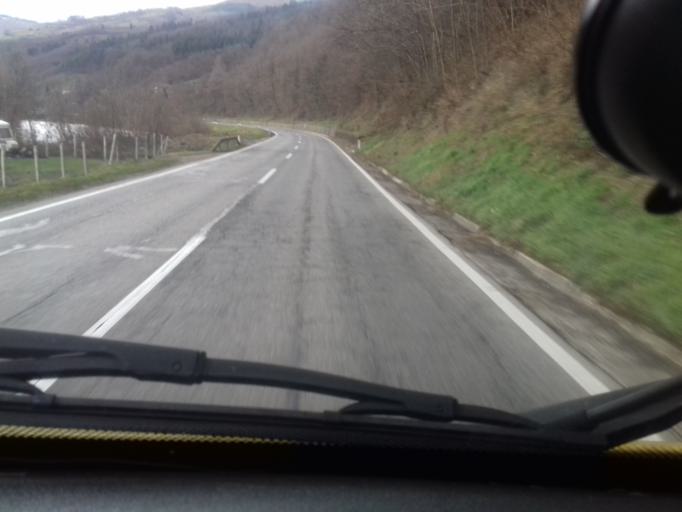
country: BA
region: Federation of Bosnia and Herzegovina
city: Zeljezno Polje
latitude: 44.3549
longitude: 17.9595
